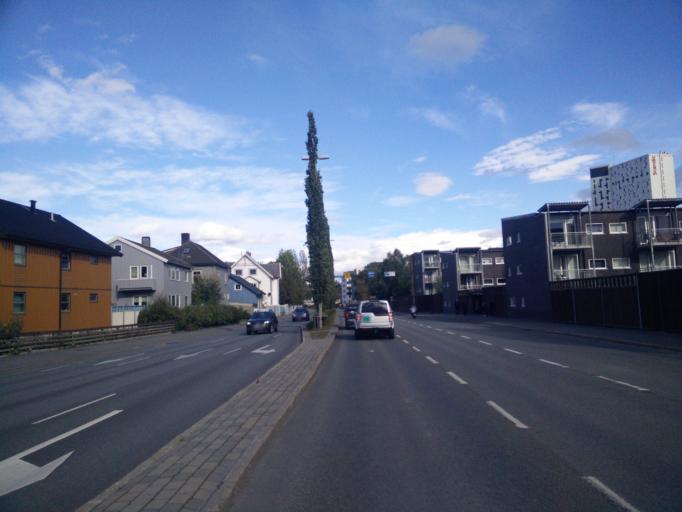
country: NO
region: Sor-Trondelag
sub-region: Trondheim
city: Trondheim
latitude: 63.4089
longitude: 10.3988
